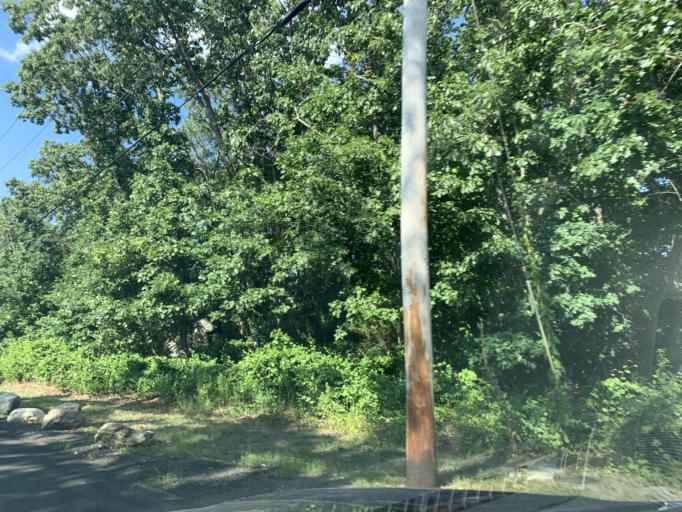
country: US
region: Rhode Island
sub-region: Washington County
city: North Kingstown
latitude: 41.6017
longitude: -71.4282
